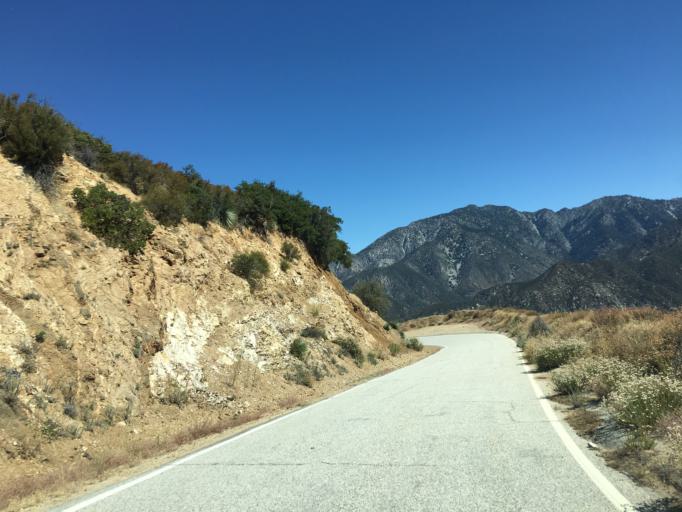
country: US
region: California
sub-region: San Bernardino County
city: San Antonio Heights
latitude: 34.2194
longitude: -117.7127
